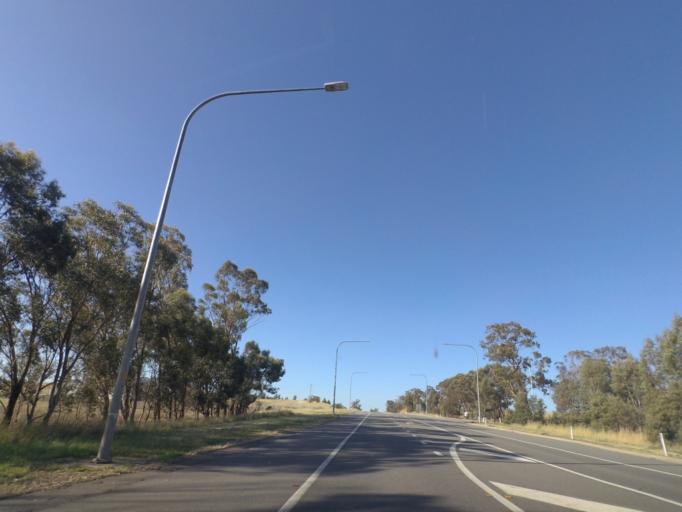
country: AU
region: New South Wales
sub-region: Wagga Wagga
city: Forest Hill
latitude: -35.2682
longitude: 147.7455
